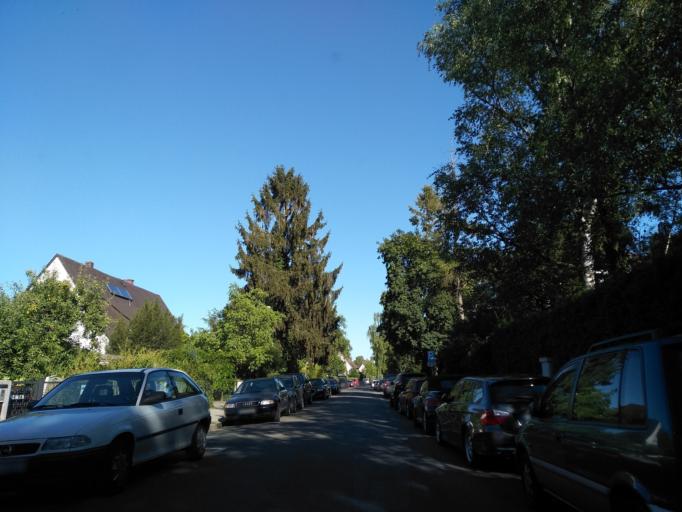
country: DE
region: Bavaria
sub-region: Regierungsbezirk Mittelfranken
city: Erlangen
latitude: 49.6006
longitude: 11.0197
